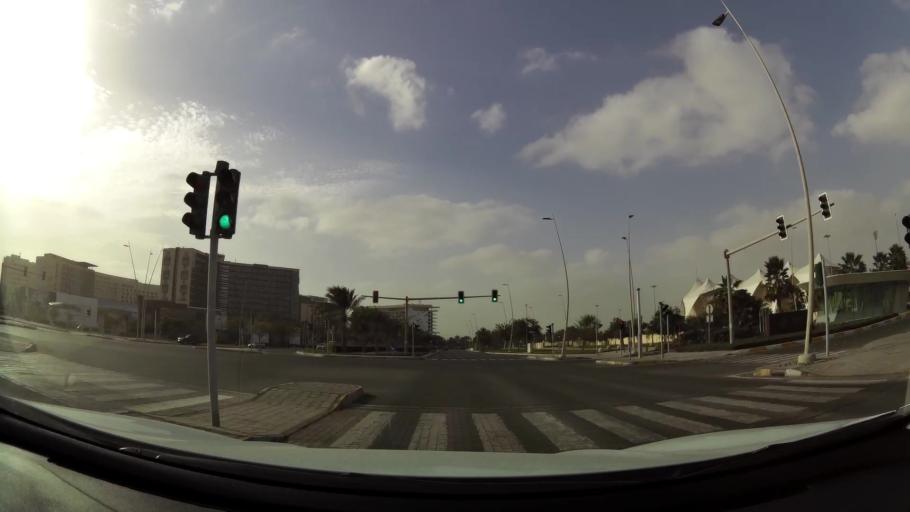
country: AE
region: Abu Dhabi
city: Abu Dhabi
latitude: 24.4659
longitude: 54.6017
